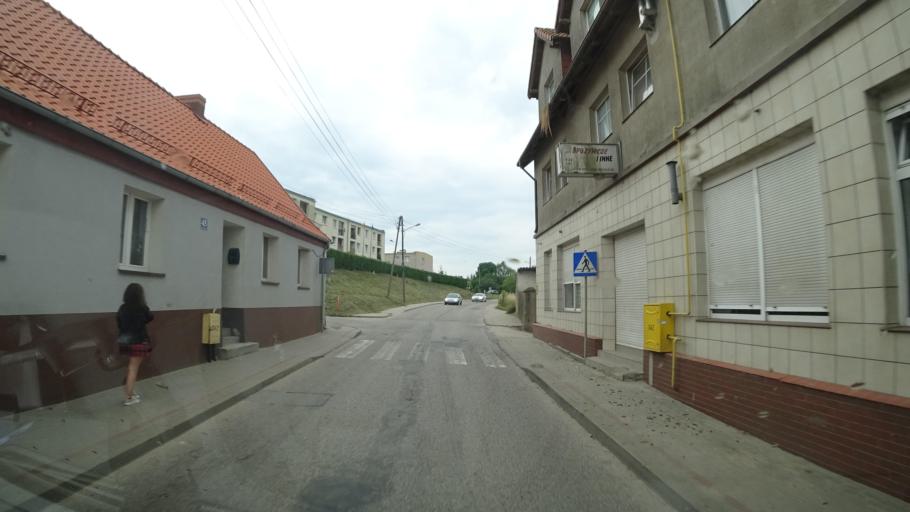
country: PL
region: Warmian-Masurian Voivodeship
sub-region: Powiat gizycki
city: Ryn
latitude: 53.9346
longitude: 21.5489
